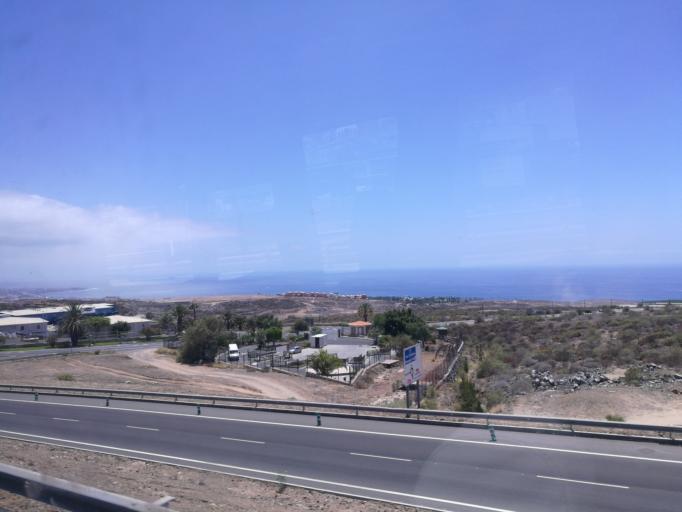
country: ES
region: Canary Islands
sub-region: Provincia de Santa Cruz de Tenerife
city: Adeje
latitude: 28.1285
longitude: -16.7453
